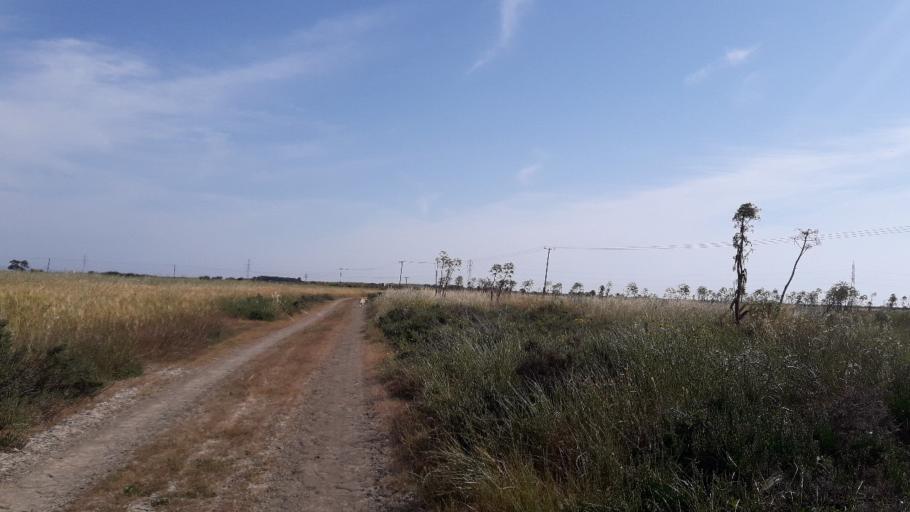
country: CY
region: Ammochostos
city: Famagusta
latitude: 35.1651
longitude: 33.8920
